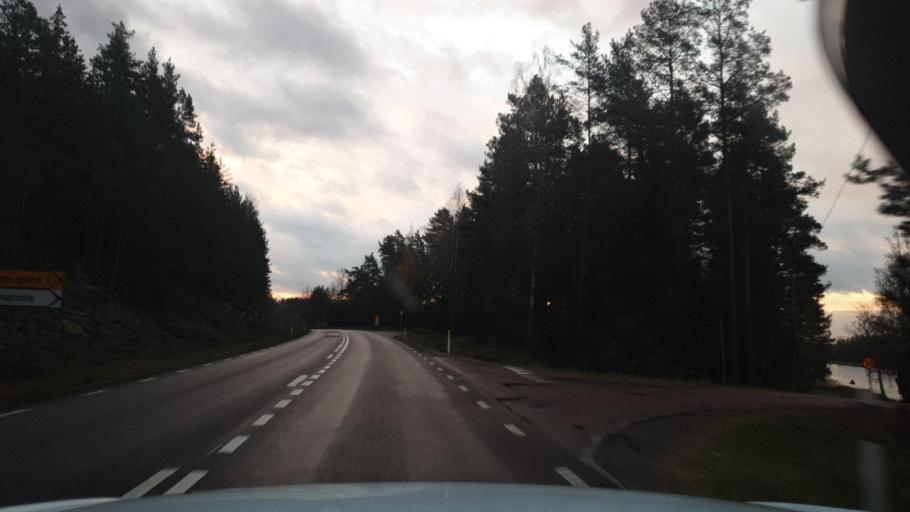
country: SE
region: Vaermland
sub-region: Arvika Kommun
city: Arvika
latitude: 59.7276
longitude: 12.4990
